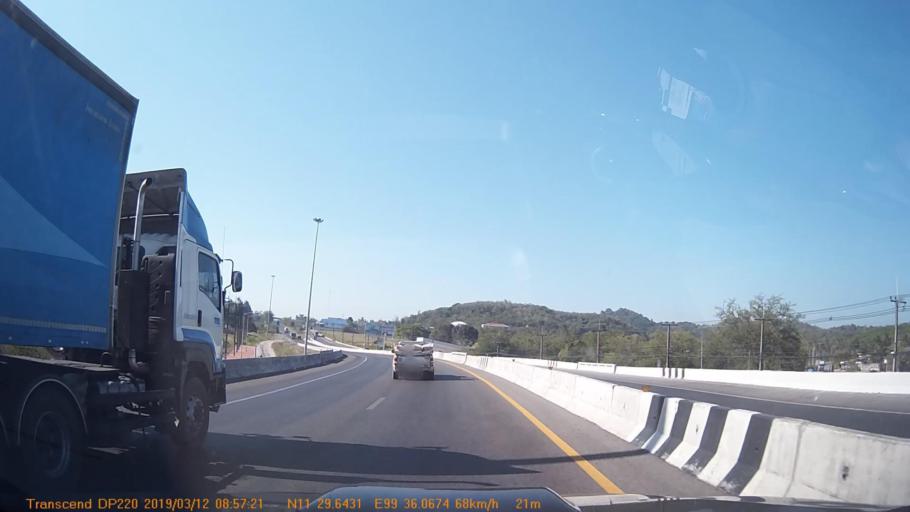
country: TH
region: Prachuap Khiri Khan
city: Thap Sakae
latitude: 11.4945
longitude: 99.6008
